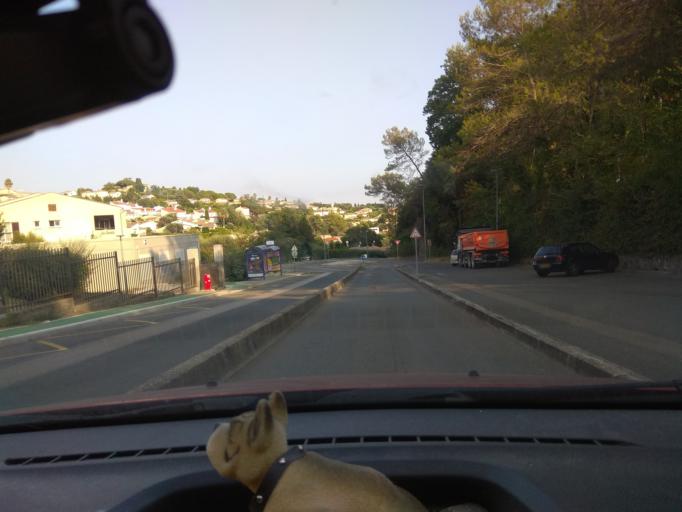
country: FR
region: Provence-Alpes-Cote d'Azur
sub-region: Departement des Alpes-Maritimes
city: La Colle-sur-Loup
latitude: 43.6842
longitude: 7.1030
